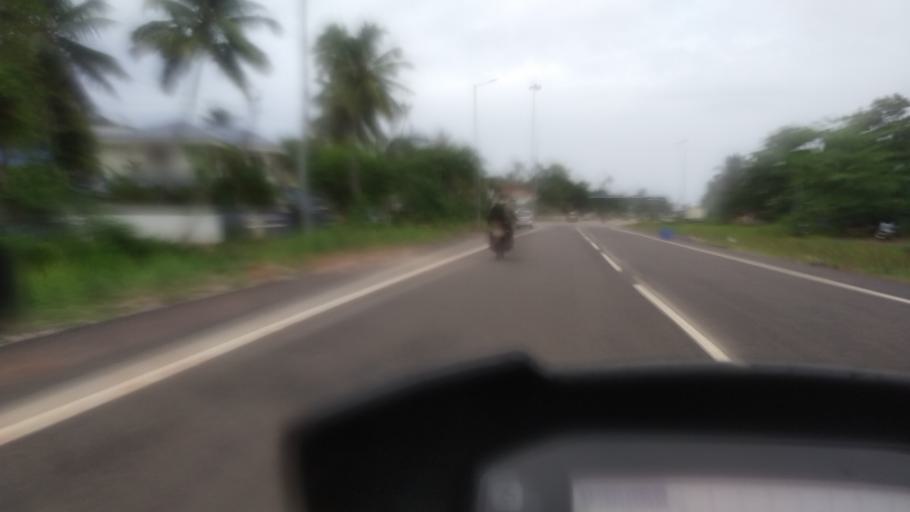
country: IN
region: Kerala
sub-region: Alappuzha
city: Alleppey
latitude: 9.5137
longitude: 76.3273
